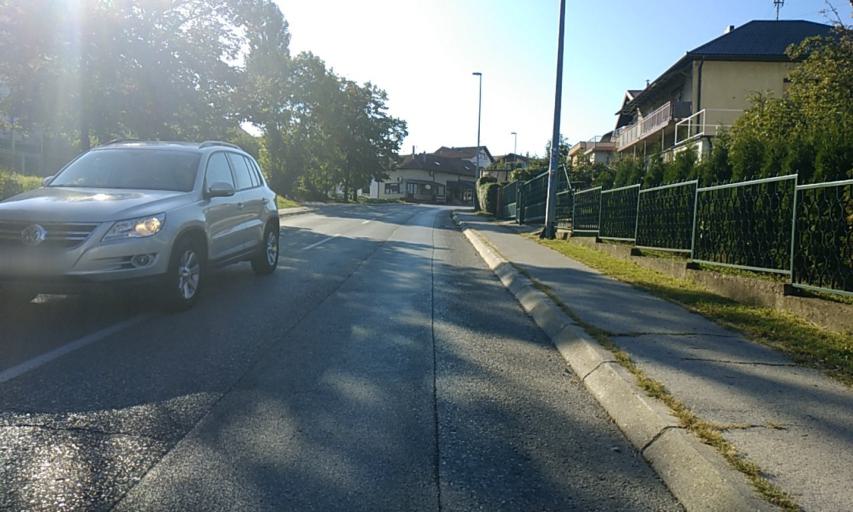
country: BA
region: Republika Srpska
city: Banja Luka
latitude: 44.7792
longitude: 17.1836
